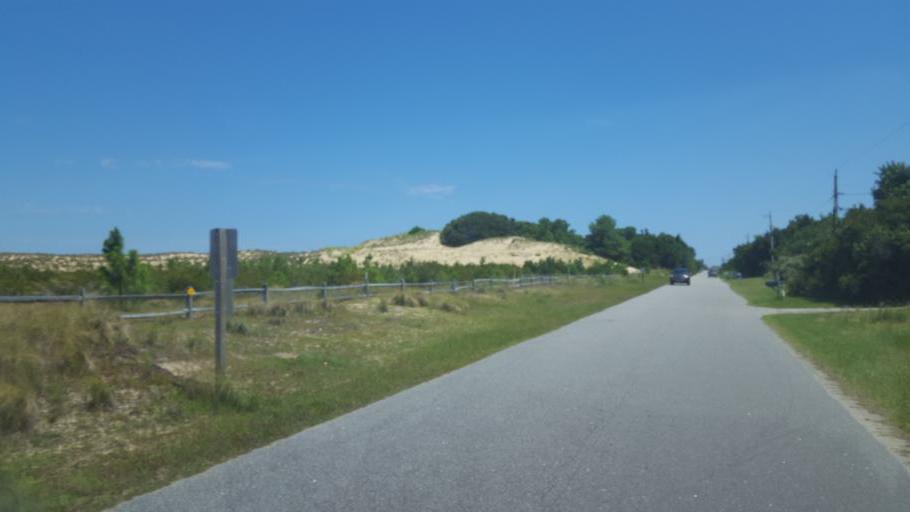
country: US
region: North Carolina
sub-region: Dare County
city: Nags Head
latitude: 35.9528
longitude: -75.6303
